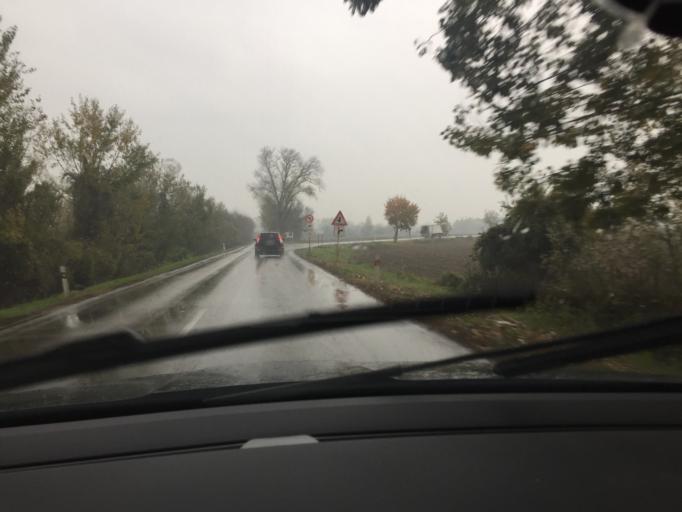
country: SK
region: Nitriansky
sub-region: Okres Nove Zamky
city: Sturovo
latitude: 47.8114
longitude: 18.7223
